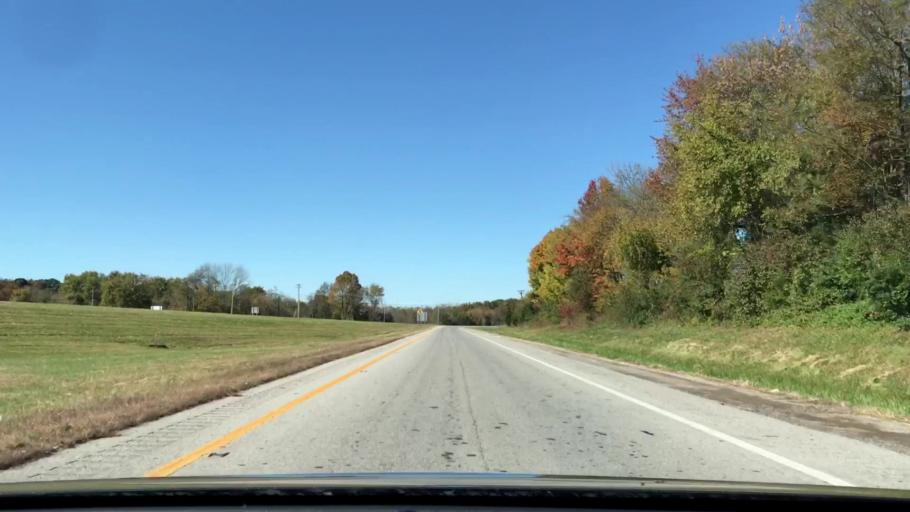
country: US
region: Kentucky
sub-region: Barren County
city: Glasgow
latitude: 36.9794
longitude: -85.9354
